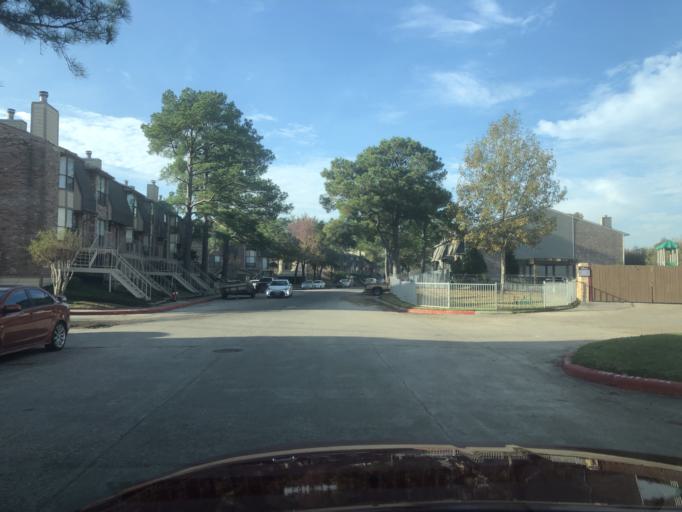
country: US
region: Texas
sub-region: Harris County
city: Spring
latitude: 30.0186
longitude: -95.4699
